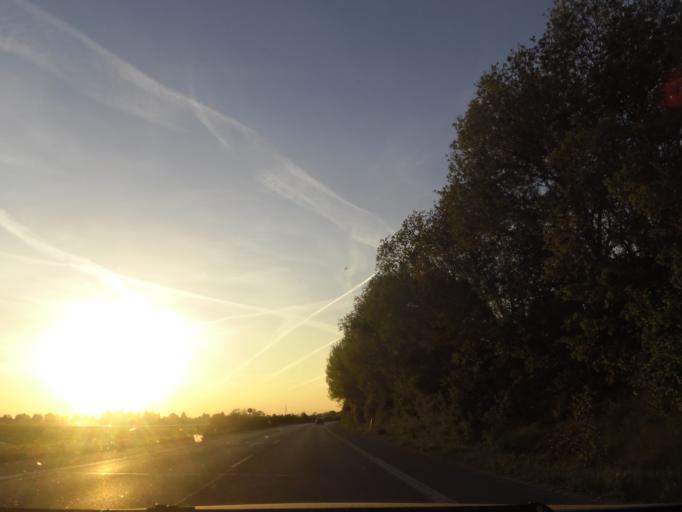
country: DE
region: Hesse
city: Weiterstadt
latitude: 49.9250
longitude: 8.5981
